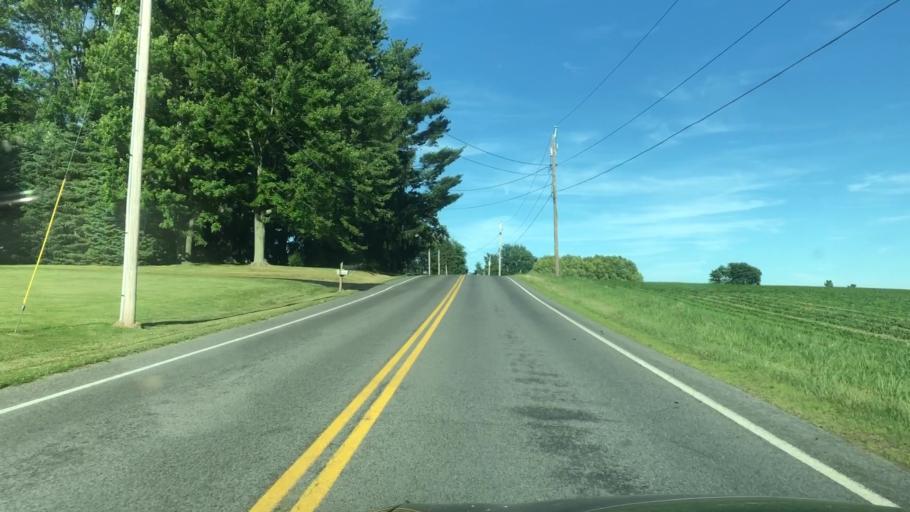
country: US
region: New York
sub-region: Wayne County
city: Macedon
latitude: 43.1163
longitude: -77.3192
